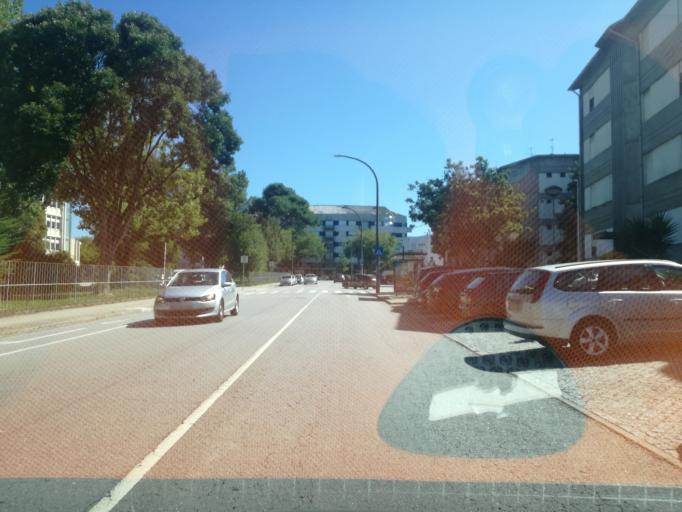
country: PT
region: Porto
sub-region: Matosinhos
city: Sao Mamede de Infesta
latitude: 41.1786
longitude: -8.6093
